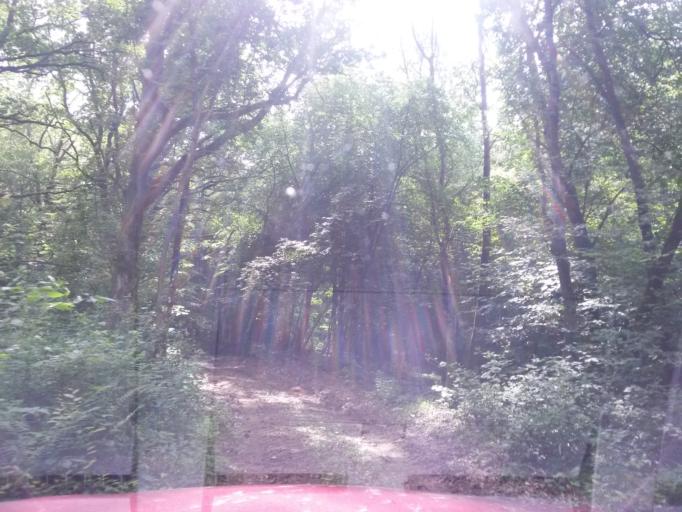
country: SK
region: Kosicky
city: Moldava nad Bodvou
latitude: 48.6485
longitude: 21.1047
